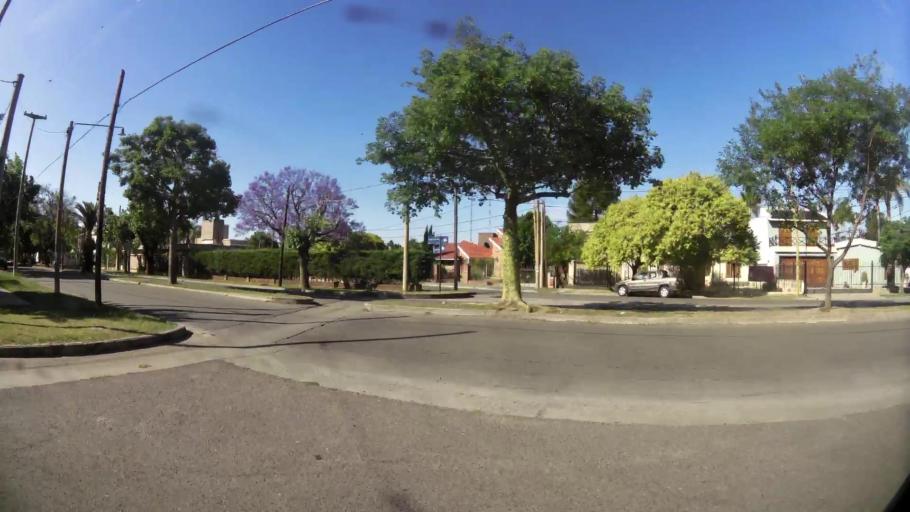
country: AR
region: Cordoba
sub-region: Departamento de Capital
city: Cordoba
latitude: -31.3610
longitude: -64.1998
